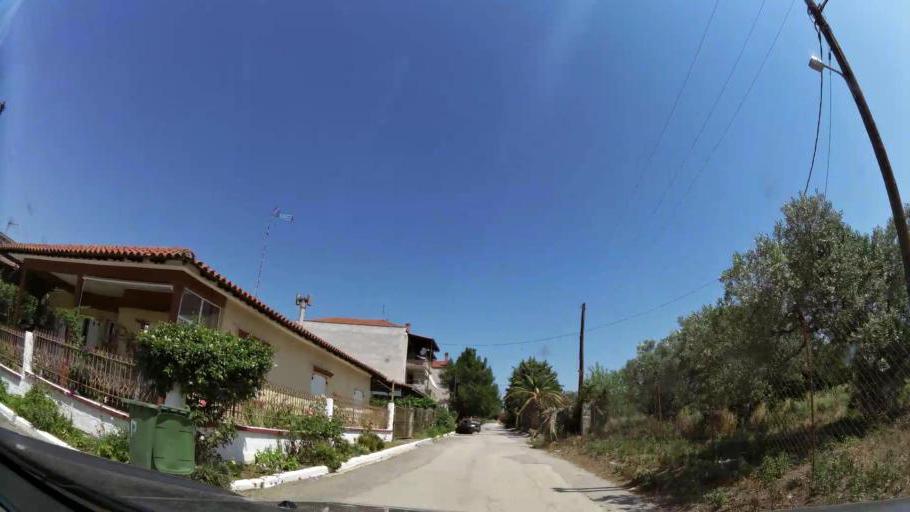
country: GR
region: Central Macedonia
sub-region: Nomos Thessalonikis
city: Agia Triada
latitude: 40.4977
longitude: 22.8367
